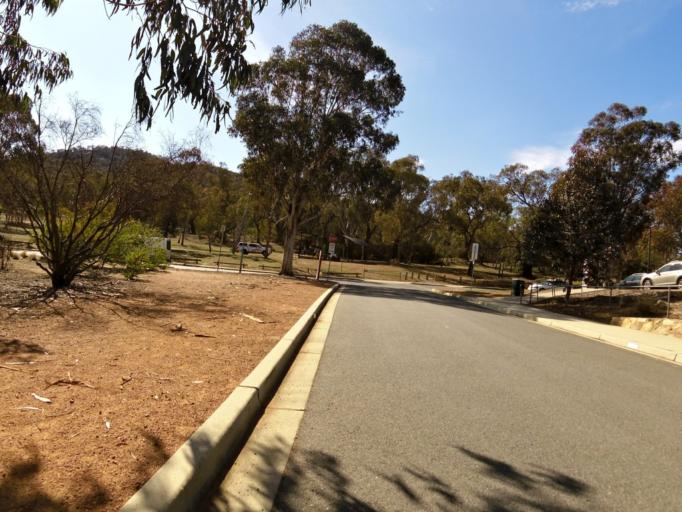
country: AU
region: Australian Capital Territory
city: Canberra
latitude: -35.2804
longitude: 149.1501
